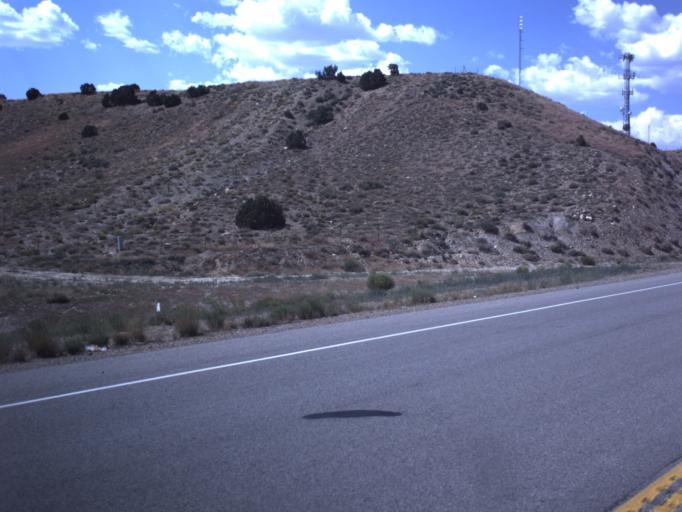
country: US
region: Utah
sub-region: Carbon County
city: Price
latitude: 39.5423
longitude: -110.8146
